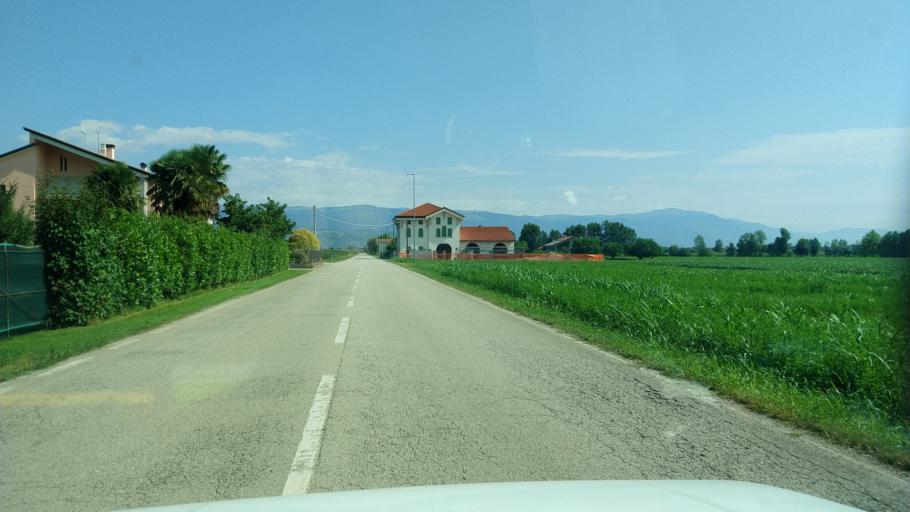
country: IT
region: Veneto
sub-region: Provincia di Vicenza
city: Sandrigo
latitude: 45.6710
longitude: 11.6079
